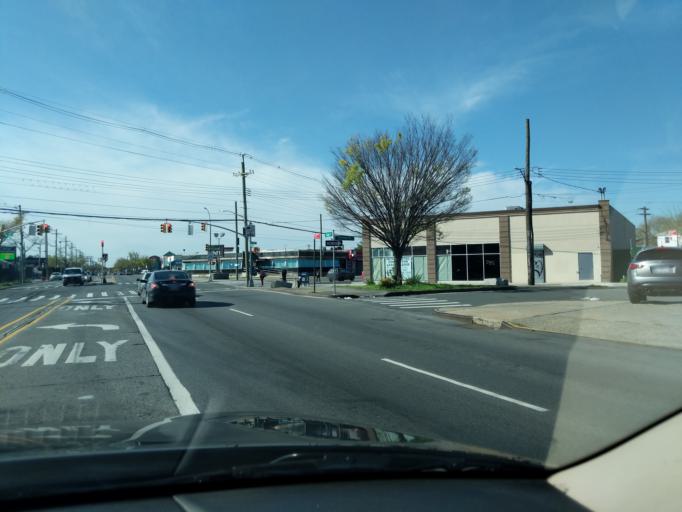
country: US
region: New York
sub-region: Kings County
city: Brooklyn
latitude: 40.6326
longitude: -73.9187
